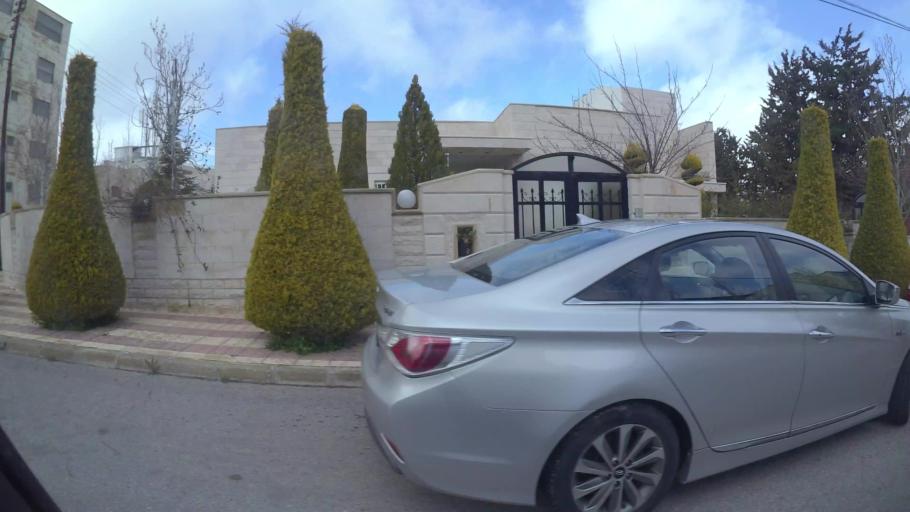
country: JO
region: Amman
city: Al Jubayhah
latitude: 32.0419
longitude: 35.8721
